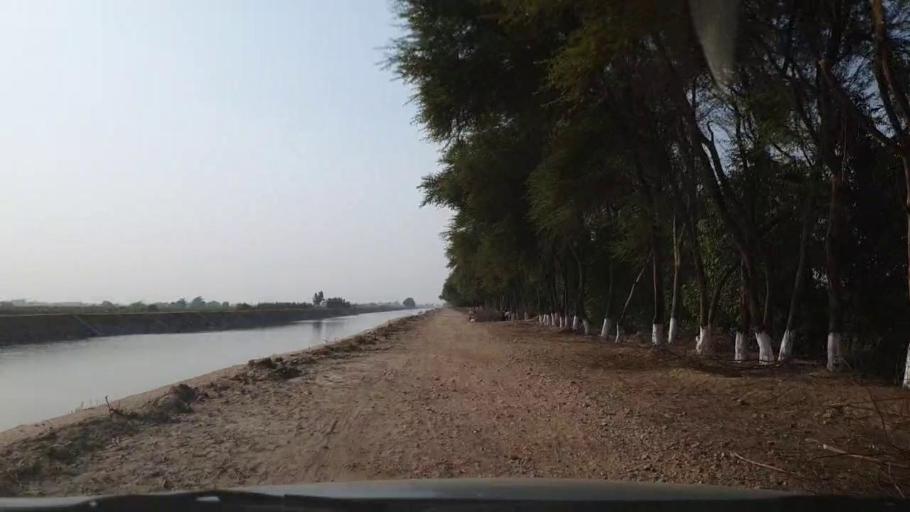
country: PK
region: Sindh
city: Tando Adam
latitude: 25.6397
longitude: 68.5876
